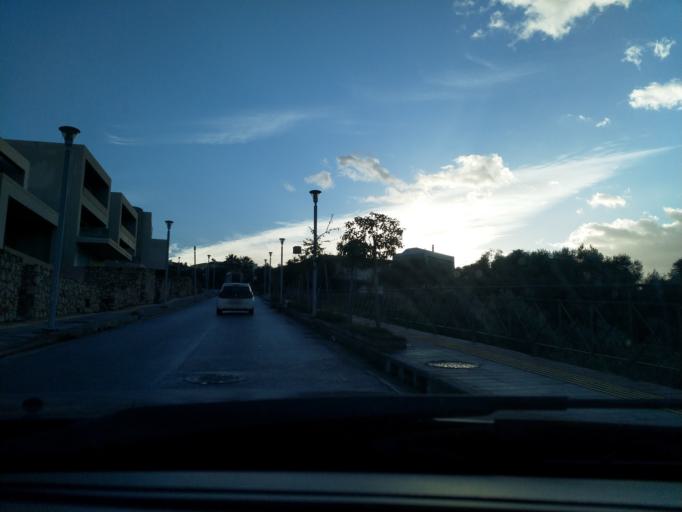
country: GR
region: Crete
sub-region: Nomos Chanias
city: Chania
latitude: 35.5121
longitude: 24.0463
